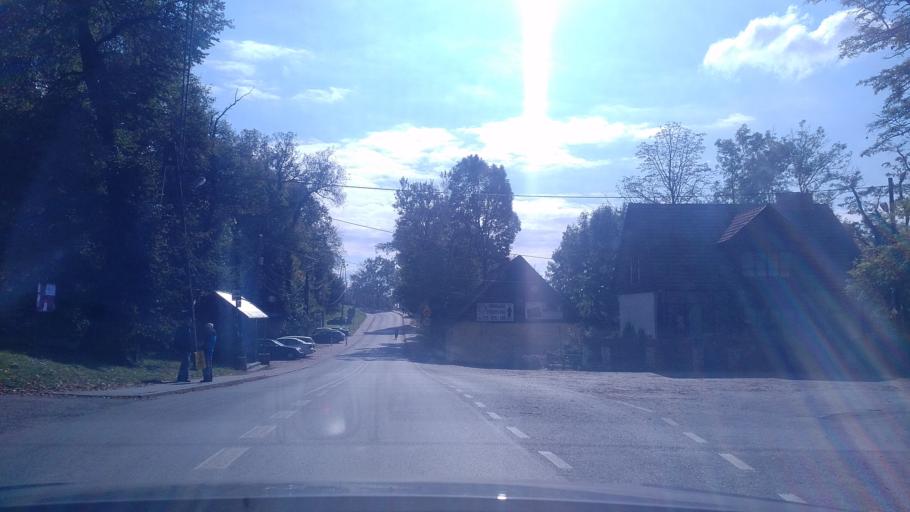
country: PL
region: Lesser Poland Voivodeship
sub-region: Powiat krakowski
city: Modlnica
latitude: 50.1310
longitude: 19.8631
